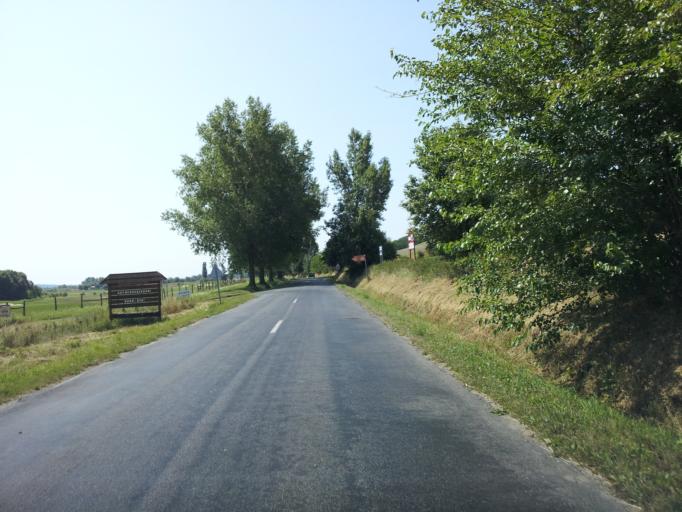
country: HU
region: Zala
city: Heviz
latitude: 46.8293
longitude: 17.0926
